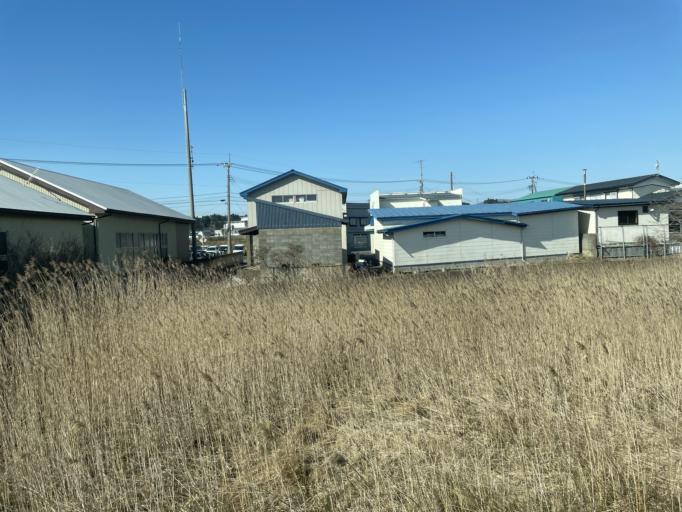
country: JP
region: Aomori
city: Hachinohe
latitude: 40.4130
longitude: 141.7142
